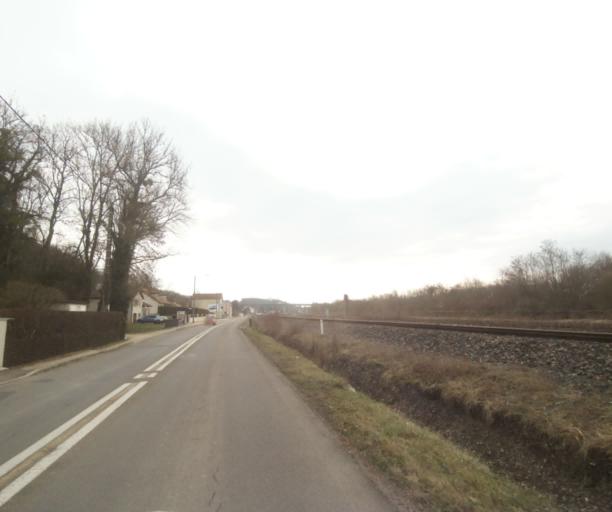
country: FR
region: Champagne-Ardenne
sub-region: Departement de la Haute-Marne
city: Bettancourt-la-Ferree
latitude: 48.6319
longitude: 4.9851
